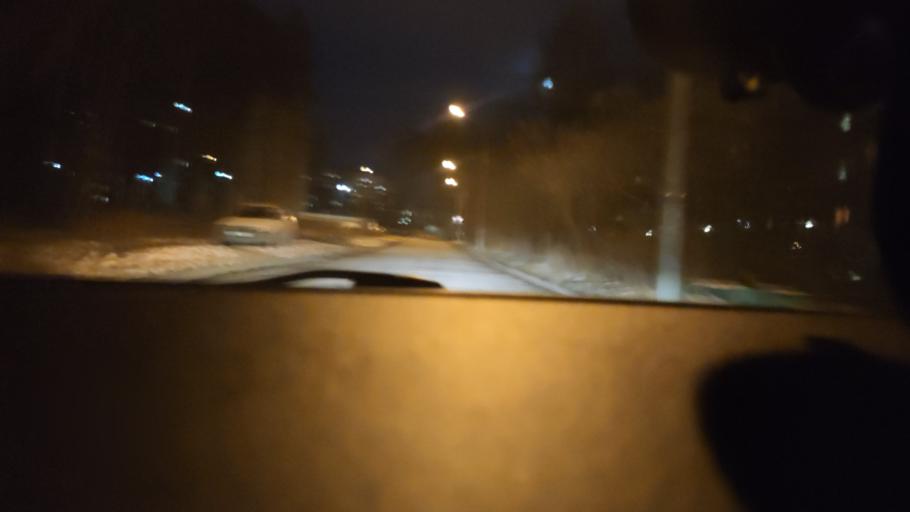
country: RU
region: Perm
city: Kondratovo
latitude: 58.0287
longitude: 56.0122
